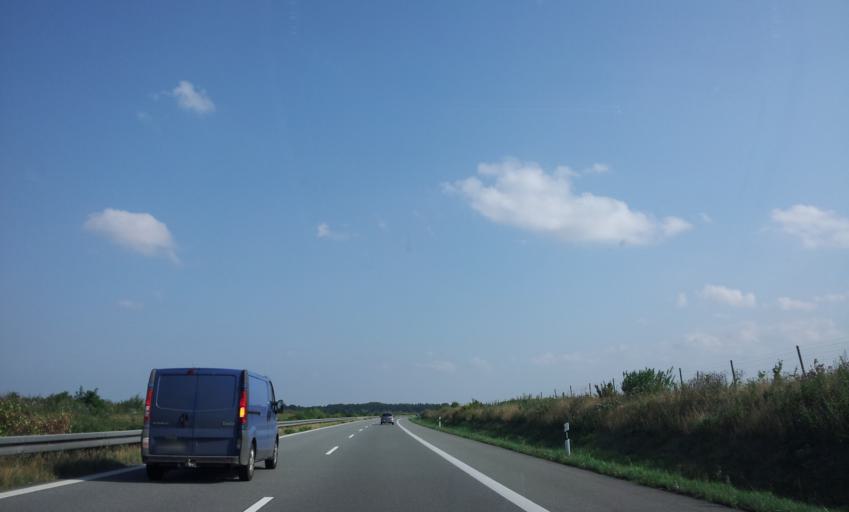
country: DE
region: Mecklenburg-Vorpommern
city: Jarmen
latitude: 53.9757
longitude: 13.3582
